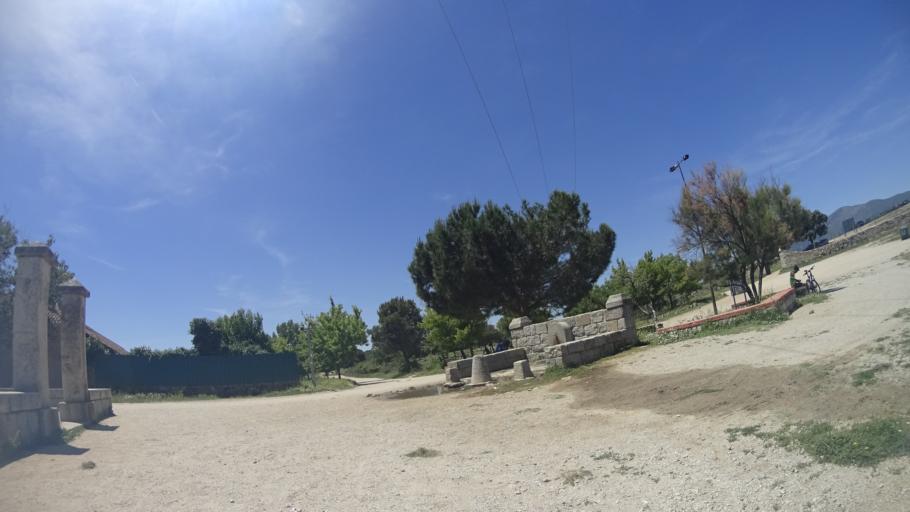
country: ES
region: Madrid
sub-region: Provincia de Madrid
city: Navalquejigo
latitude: 40.6113
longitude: -4.0362
